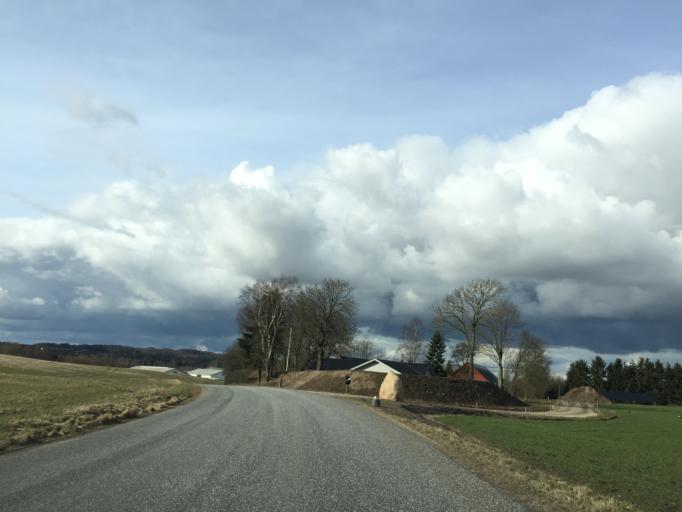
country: DK
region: Central Jutland
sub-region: Favrskov Kommune
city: Hammel
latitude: 56.2176
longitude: 9.7483
